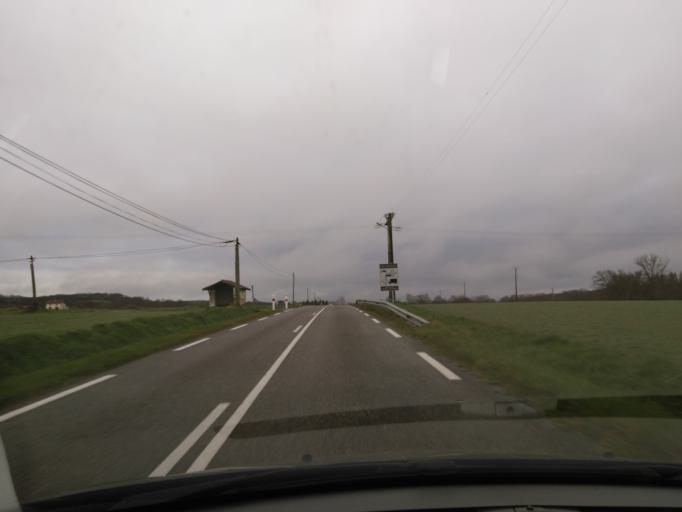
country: FR
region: Midi-Pyrenees
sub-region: Departement de la Haute-Garonne
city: Montesquieu-Volvestre
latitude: 43.1740
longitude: 1.2571
